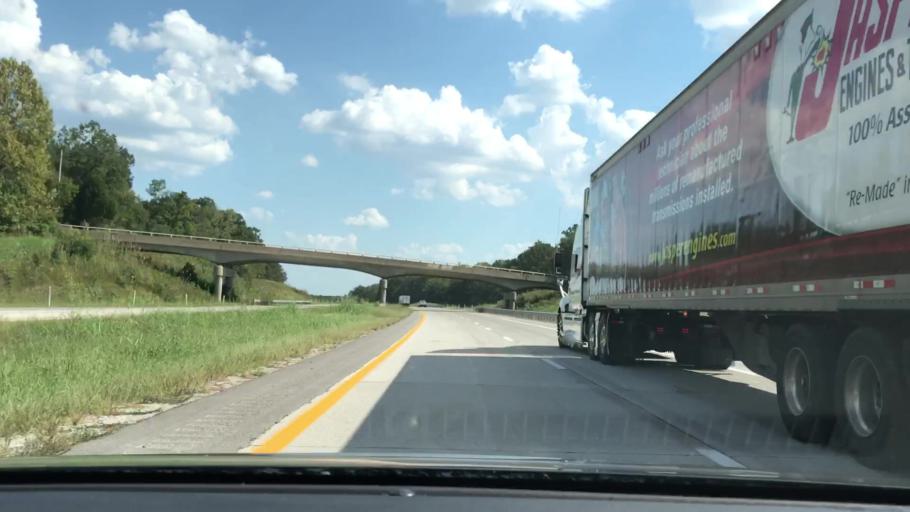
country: US
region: Kentucky
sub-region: Ohio County
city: Oak Grove
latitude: 37.3516
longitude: -86.7857
